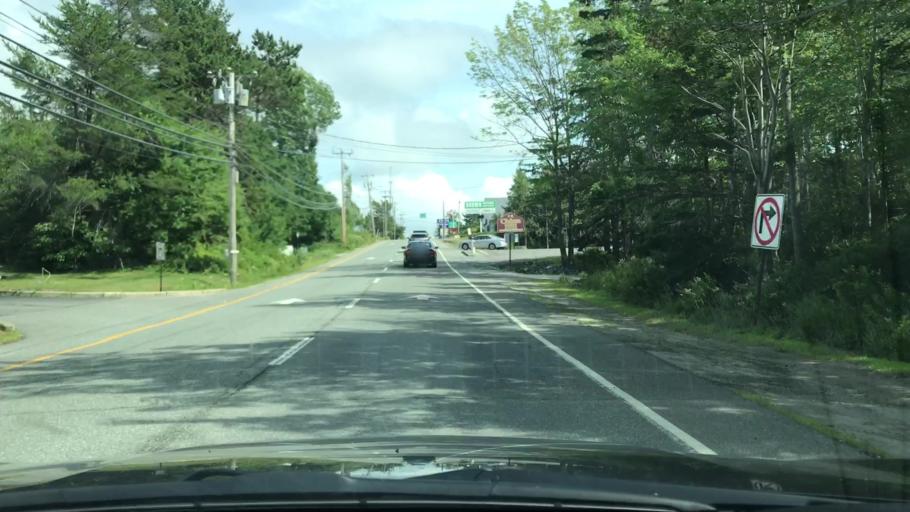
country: US
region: Maine
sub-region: Hancock County
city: Ellsworth
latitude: 44.5278
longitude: -68.4025
